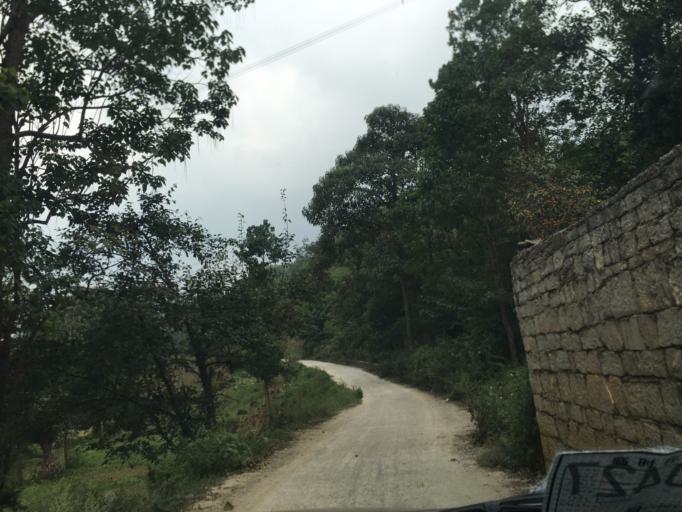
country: CN
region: Guangxi Zhuangzu Zizhiqu
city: Xinzhou
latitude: 25.5657
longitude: 105.6063
